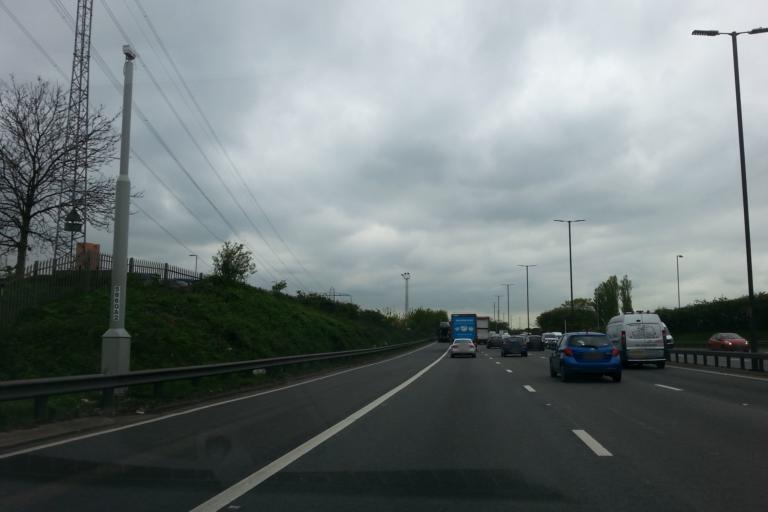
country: GB
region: England
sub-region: City and Borough of Birmingham
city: Hockley
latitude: 52.5263
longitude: -1.8894
